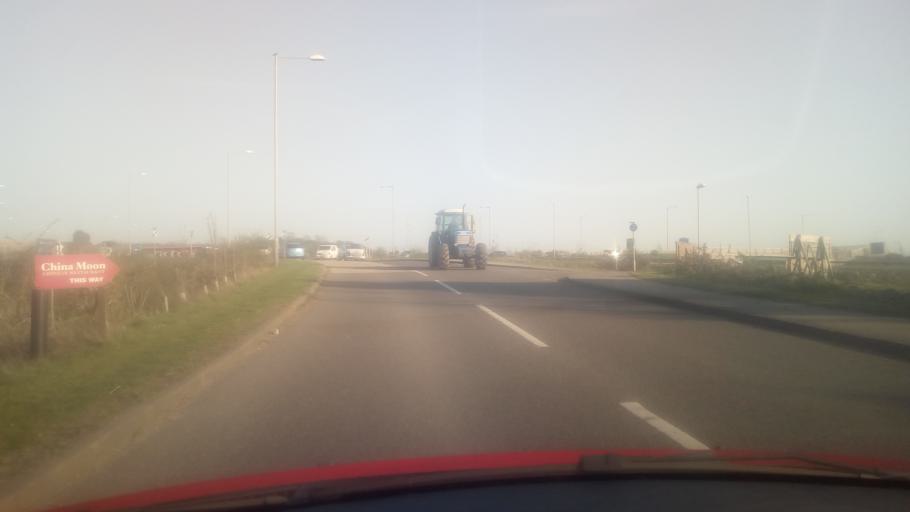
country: GB
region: England
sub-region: Nottinghamshire
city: Tuxford
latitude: 53.2569
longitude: -0.9244
